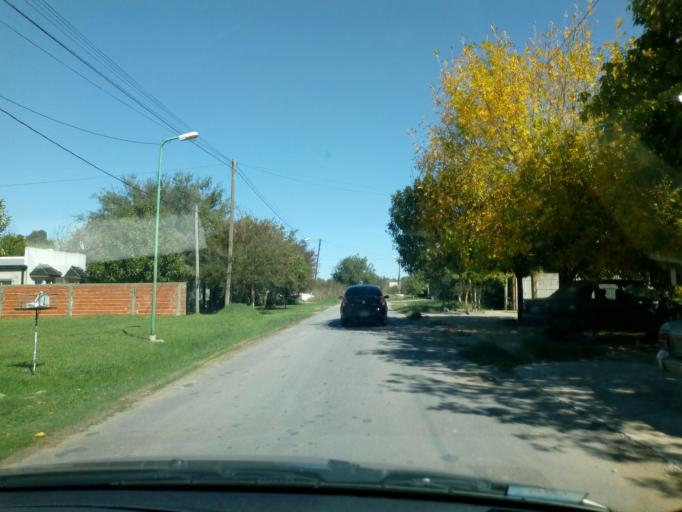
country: AR
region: Buenos Aires
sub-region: Partido de La Plata
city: La Plata
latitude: -35.0008
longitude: -58.0460
